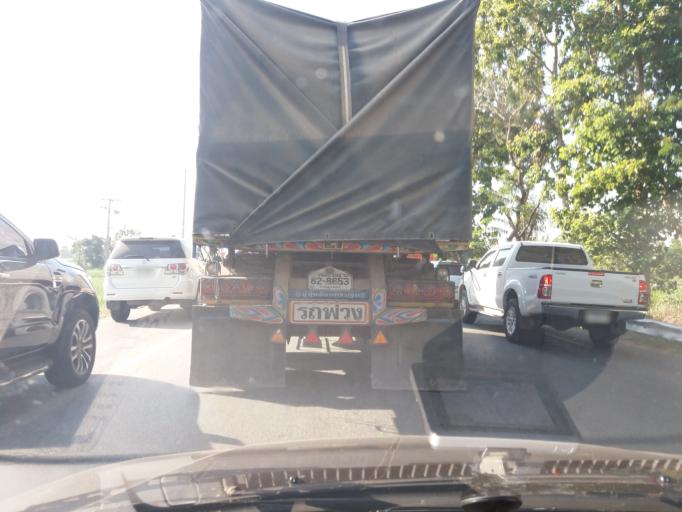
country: TH
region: Nakhon Sawan
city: Nakhon Sawan
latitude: 15.7358
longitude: 100.0239
